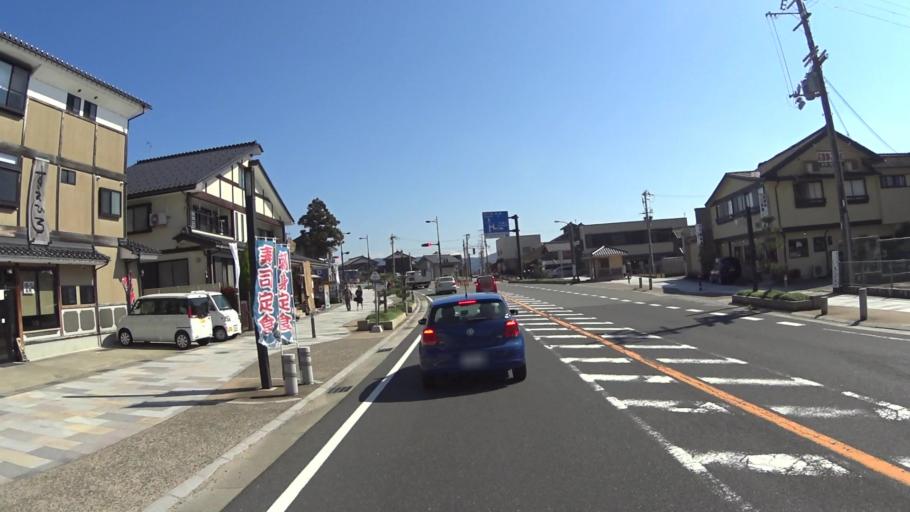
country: JP
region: Kyoto
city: Miyazu
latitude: 35.5835
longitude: 135.1874
